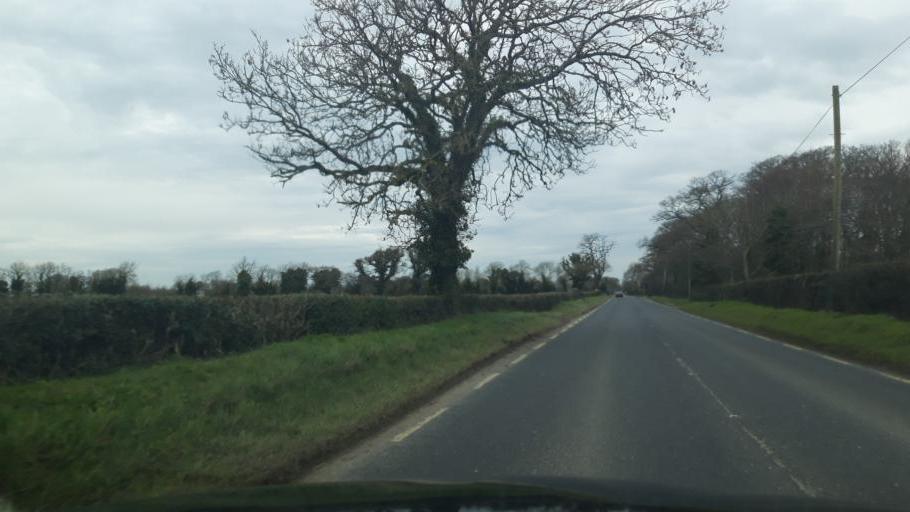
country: IE
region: Leinster
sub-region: Kildare
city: Maynooth
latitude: 53.3540
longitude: -6.5965
